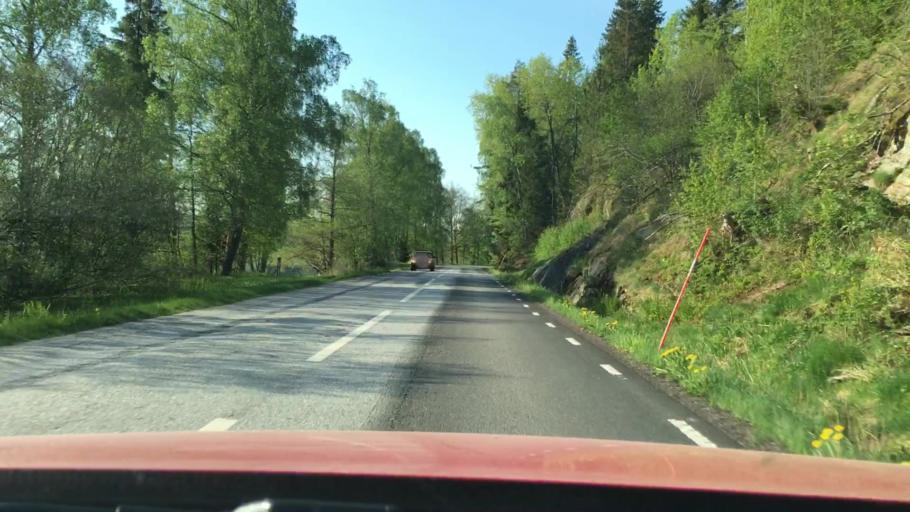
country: SE
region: Vaestra Goetaland
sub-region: Munkedals Kommun
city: Munkedal
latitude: 58.6264
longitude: 11.5596
